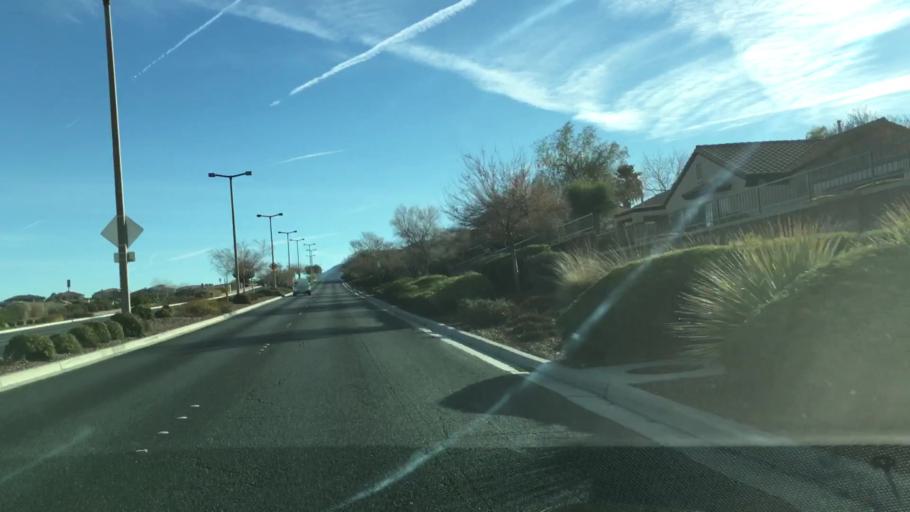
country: US
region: Nevada
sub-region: Clark County
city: Whitney
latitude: 35.9693
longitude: -115.1135
